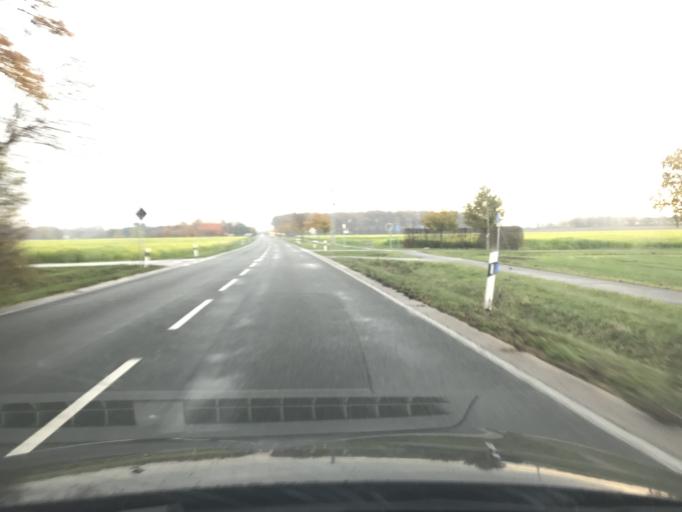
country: DE
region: North Rhine-Westphalia
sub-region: Regierungsbezirk Munster
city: Warendorf
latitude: 51.9230
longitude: 7.9261
